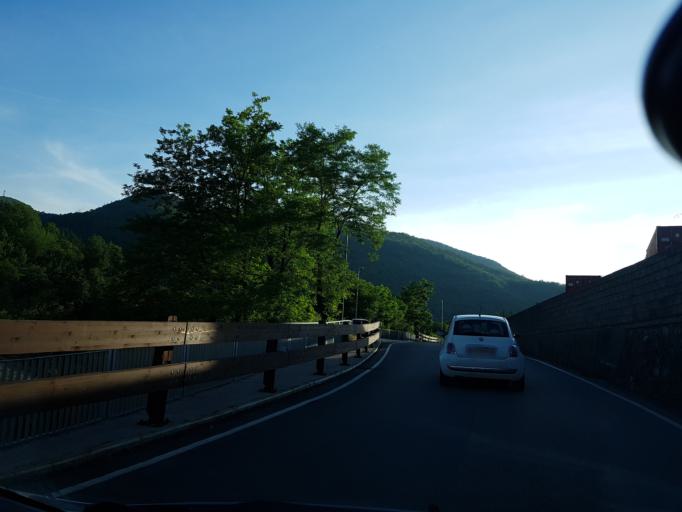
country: IT
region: Tuscany
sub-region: Provincia di Massa-Carrara
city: Casola in Lunigiana
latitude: 44.1943
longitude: 10.1956
